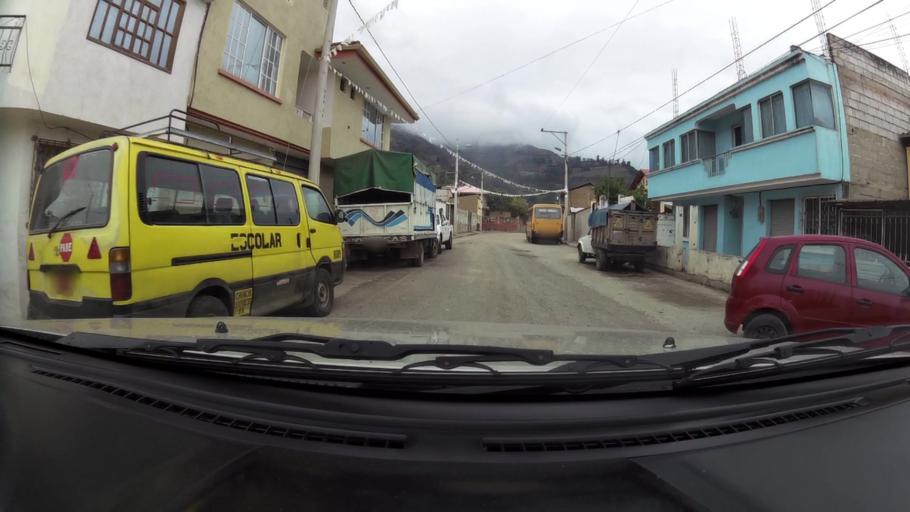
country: EC
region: Chimborazo
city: Alausi
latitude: -2.2917
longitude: -78.9206
